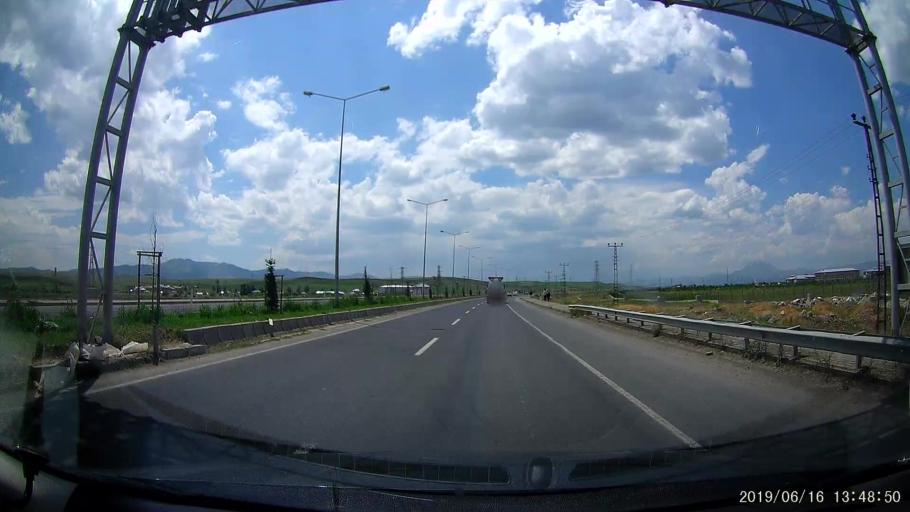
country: TR
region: Agri
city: Agri
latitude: 39.7148
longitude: 43.0001
